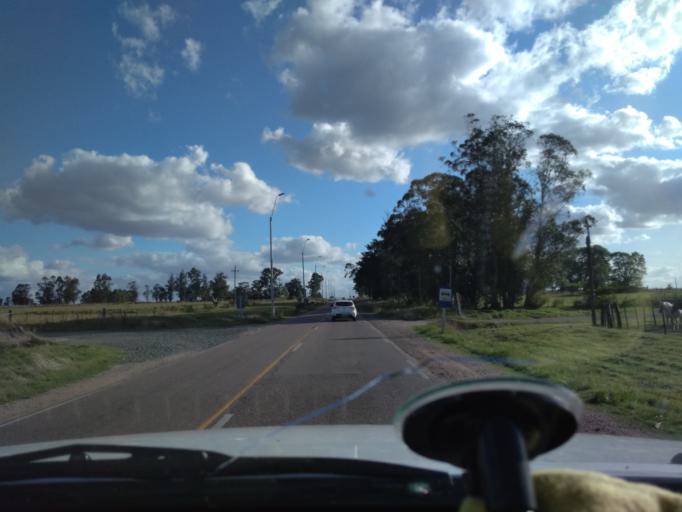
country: UY
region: Canelones
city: Tala
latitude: -34.3566
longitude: -55.7721
